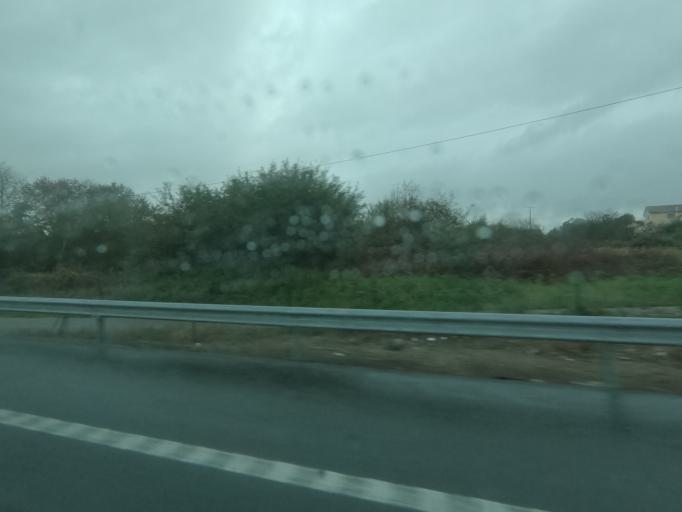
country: ES
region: Galicia
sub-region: Provincia de Pontevedra
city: Poio
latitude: 42.4062
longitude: -8.6519
